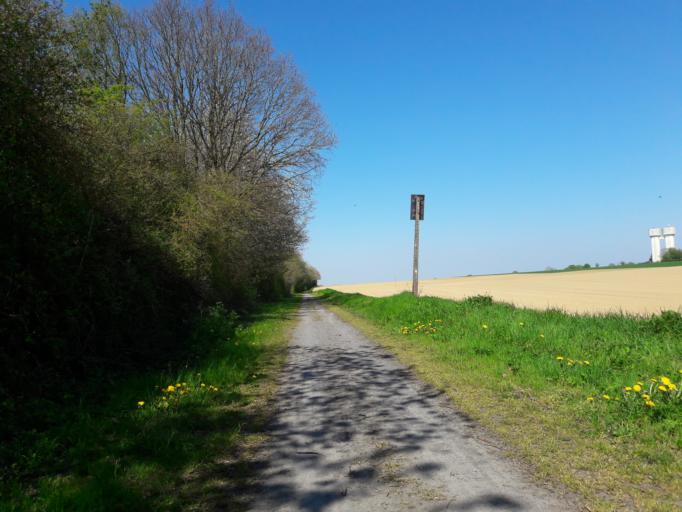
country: FR
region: Nord-Pas-de-Calais
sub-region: Departement du Nord
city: Sains-du-Nord
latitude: 50.1546
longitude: 4.0698
